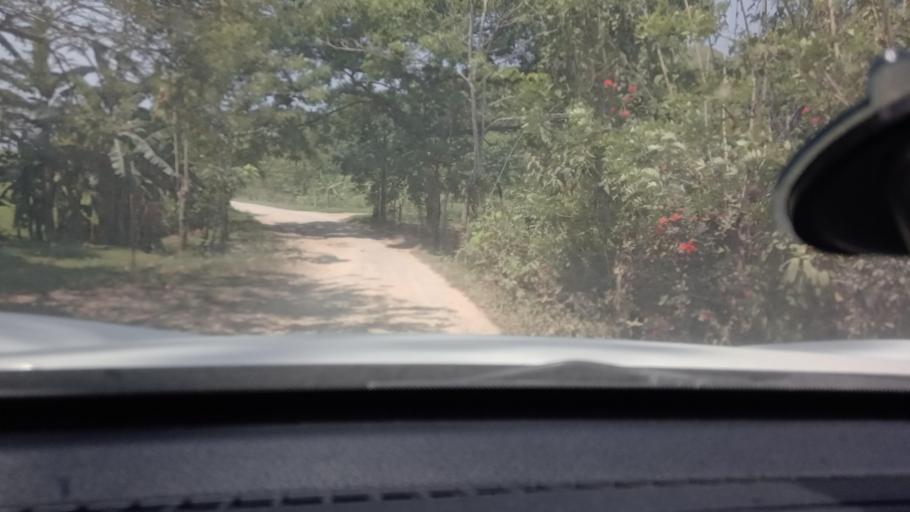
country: MX
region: Tabasco
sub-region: Huimanguillo
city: Francisco Rueda
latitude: 17.5213
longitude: -93.8856
